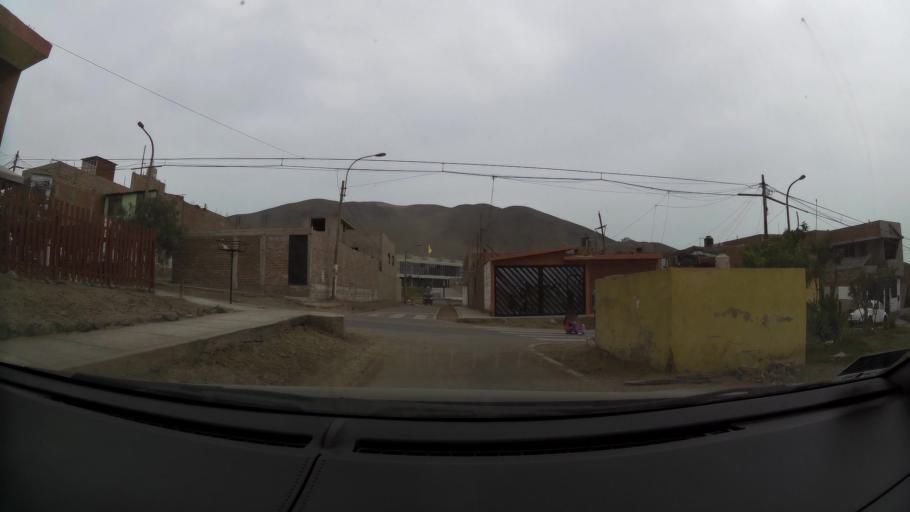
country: PE
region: Lima
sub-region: Lima
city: Santa Rosa
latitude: -11.7914
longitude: -77.1577
